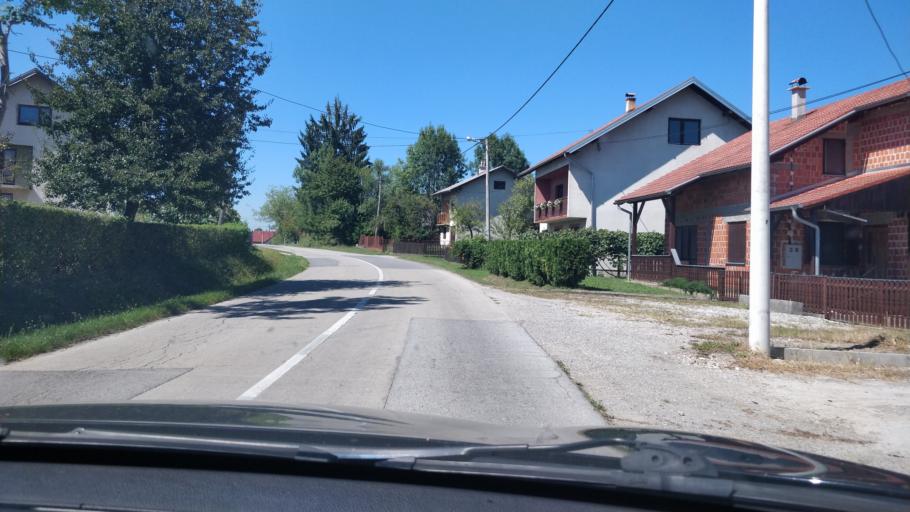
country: HR
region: Karlovacka
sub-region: Grad Karlovac
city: Karlovac
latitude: 45.4636
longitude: 15.6424
